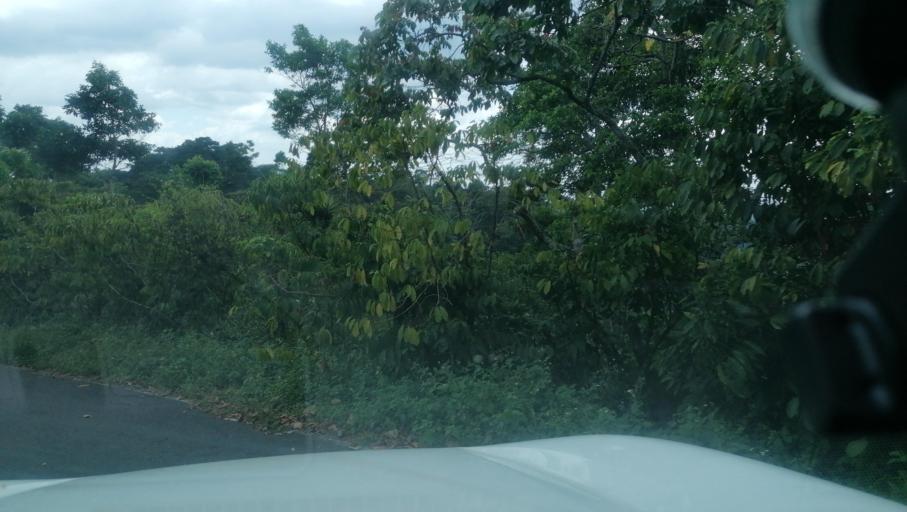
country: MX
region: Chiapas
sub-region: Cacahoatan
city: Benito Juarez
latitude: 15.0620
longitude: -92.1511
